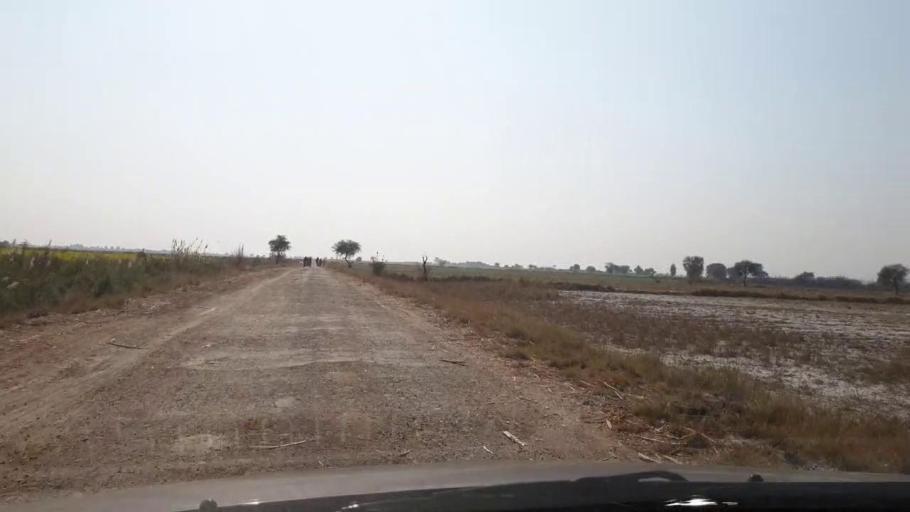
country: PK
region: Sindh
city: Jhol
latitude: 25.8775
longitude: 68.9974
